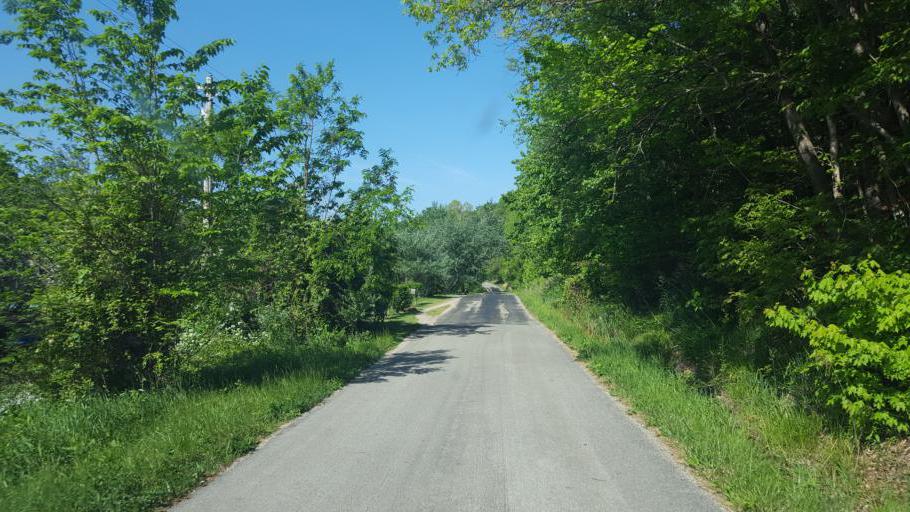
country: US
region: Ohio
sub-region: Jackson County
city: Wellston
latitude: 39.0000
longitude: -82.4863
